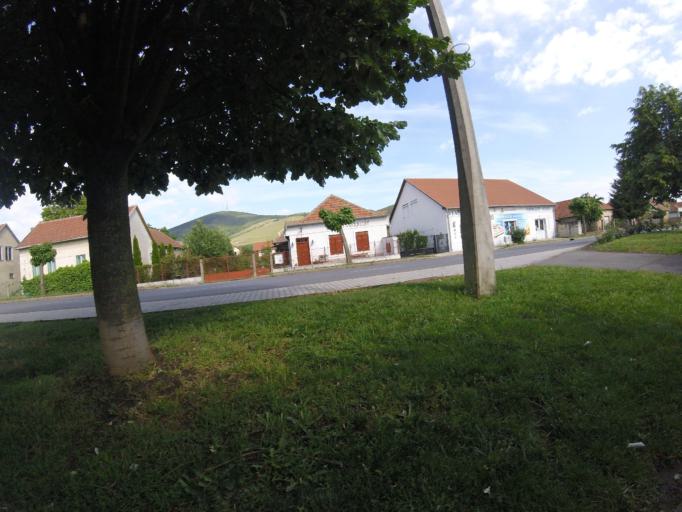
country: HU
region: Borsod-Abauj-Zemplen
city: Tokaj
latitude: 48.1085
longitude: 21.4082
